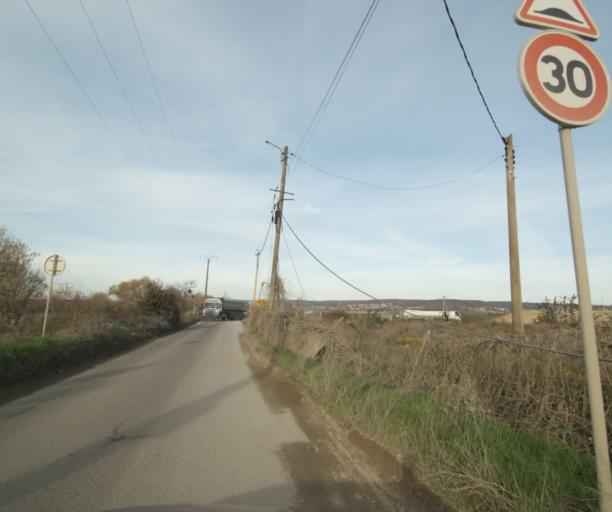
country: FR
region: Ile-de-France
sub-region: Departement des Yvelines
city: Medan
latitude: 48.9533
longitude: 2.0104
